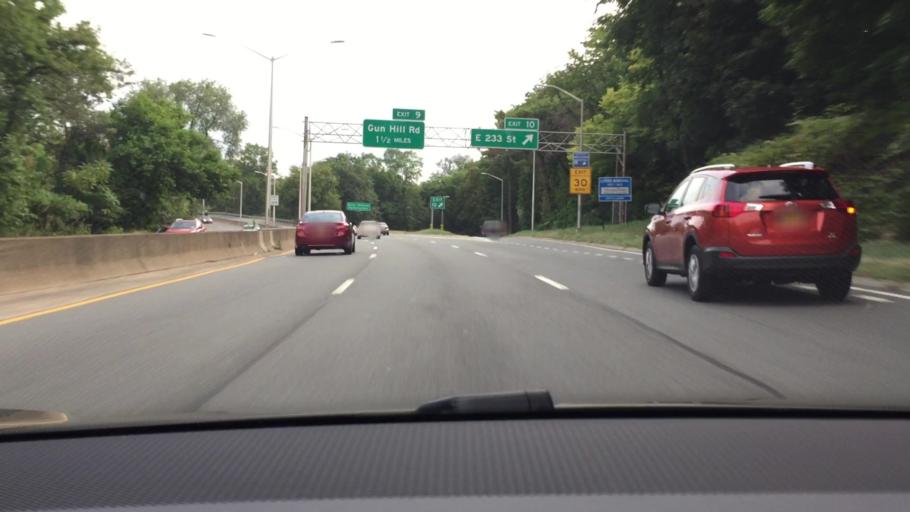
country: US
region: New York
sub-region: Westchester County
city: Mount Vernon
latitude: 40.9004
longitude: -73.8612
